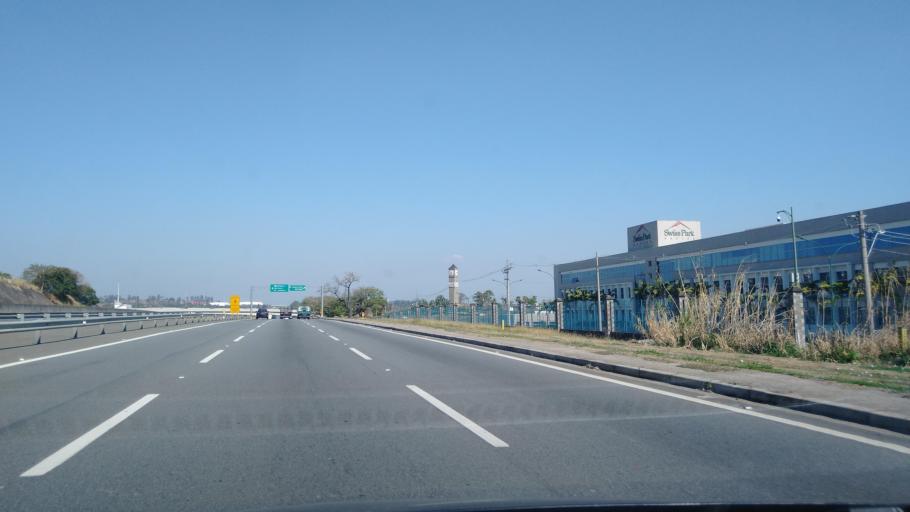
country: BR
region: Sao Paulo
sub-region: Campinas
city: Campinas
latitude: -22.9521
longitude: -47.0624
